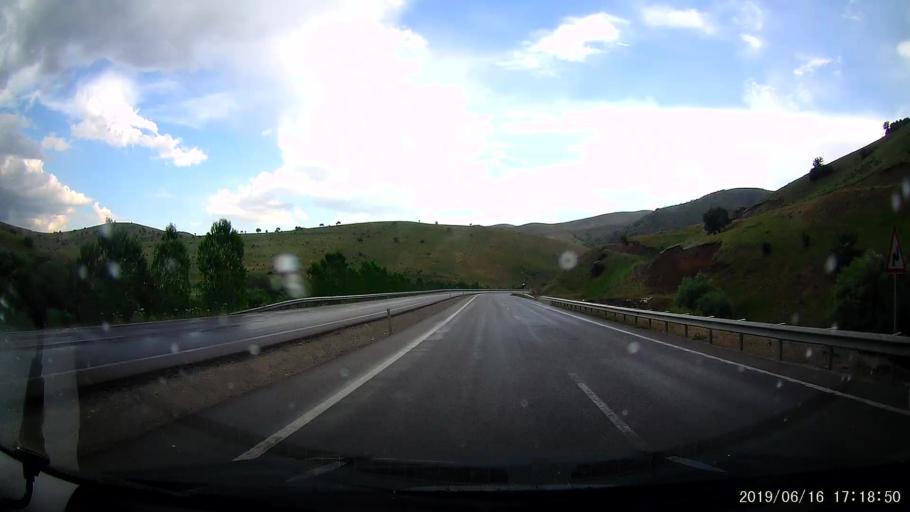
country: TR
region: Erzincan
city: Tercan
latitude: 39.8084
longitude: 40.5303
